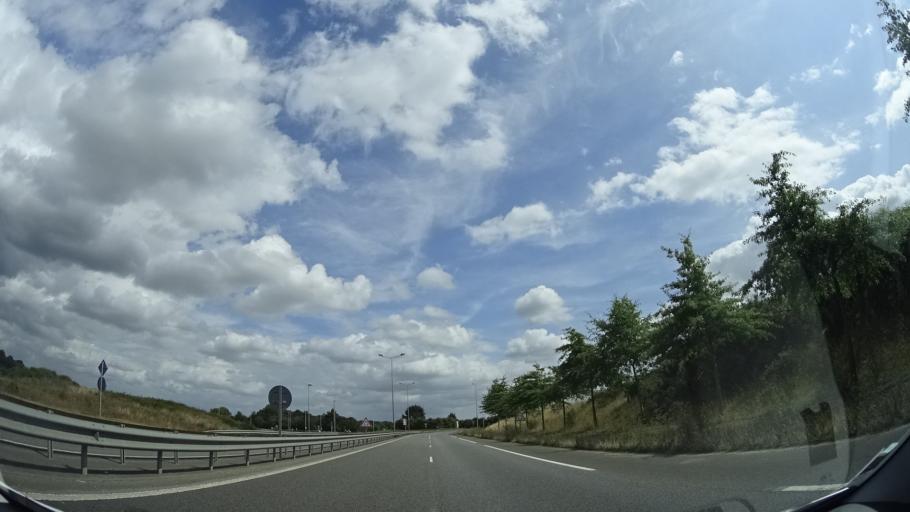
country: FR
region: Pays de la Loire
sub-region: Departement de la Mayenne
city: Saint-Berthevin
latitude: 48.0799
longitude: -0.8223
